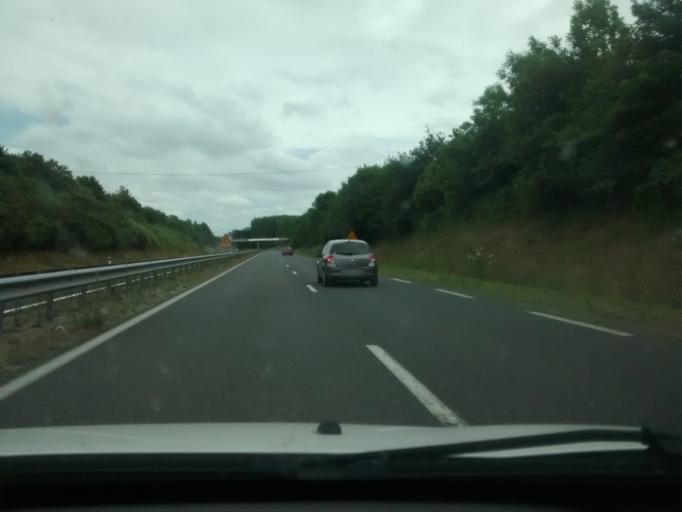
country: FR
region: Brittany
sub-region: Departement des Cotes-d'Armor
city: Cavan
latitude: 48.6719
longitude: -3.3517
